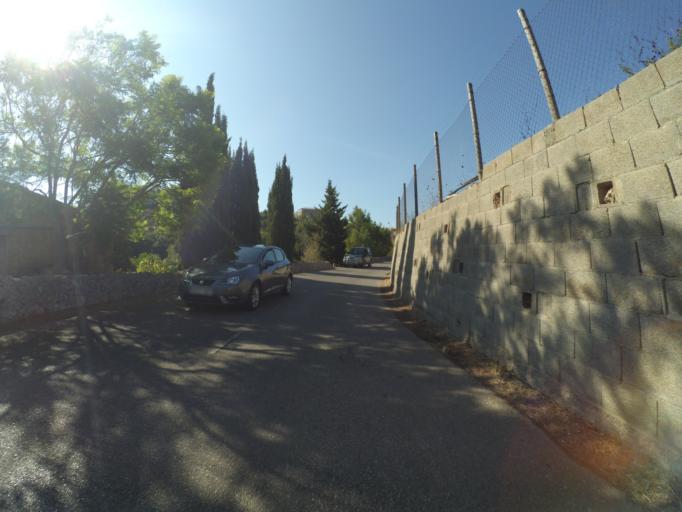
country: ES
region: Balearic Islands
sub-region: Illes Balears
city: Arta
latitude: 39.6985
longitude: 3.3517
